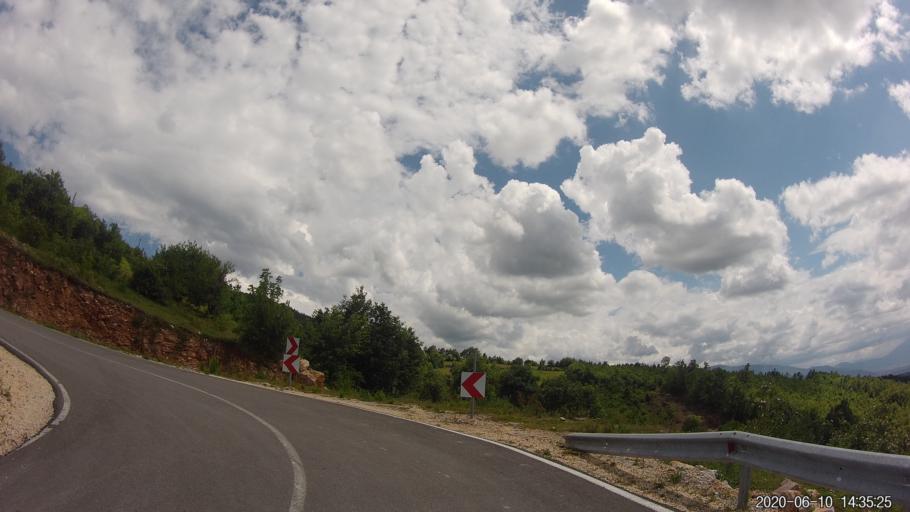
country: XK
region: Prizren
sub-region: Komuna e Therandes
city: Budakovo
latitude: 42.4130
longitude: 20.9343
